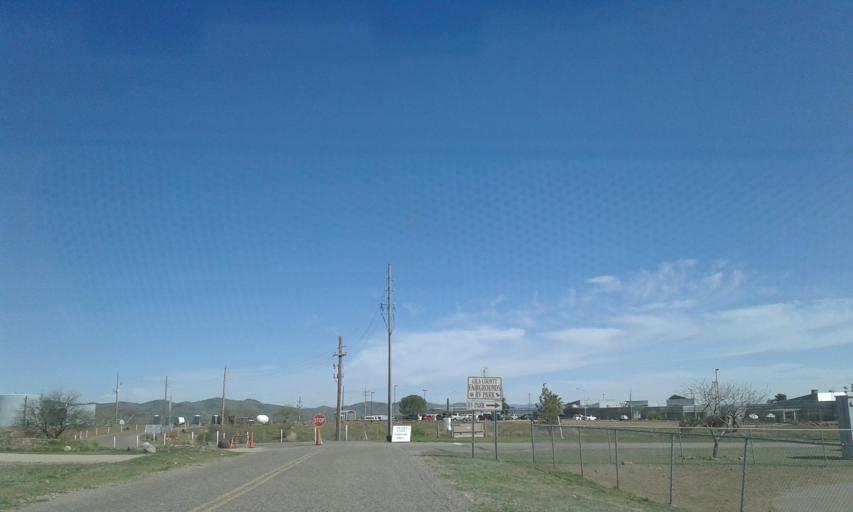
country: US
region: Arizona
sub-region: Gila County
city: Globe
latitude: 33.4181
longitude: -110.7145
